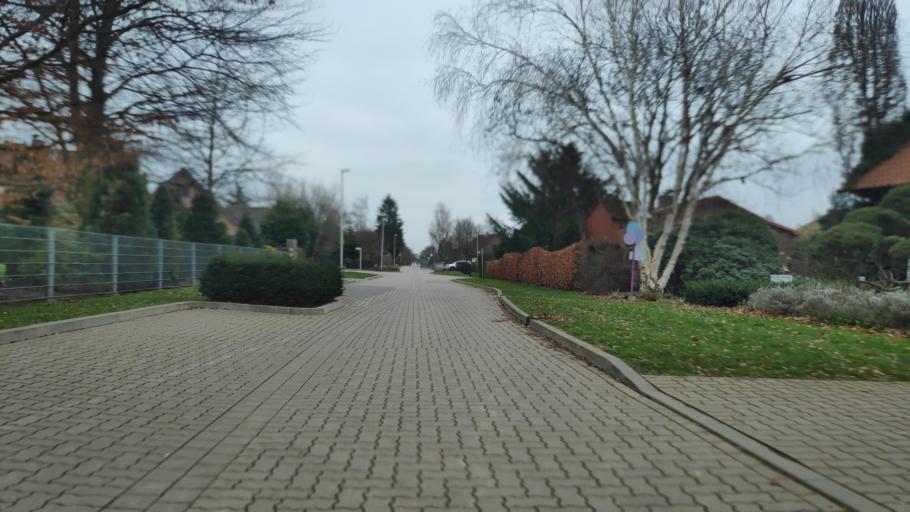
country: DE
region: North Rhine-Westphalia
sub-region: Regierungsbezirk Detmold
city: Minden
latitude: 52.2934
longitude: 8.8717
